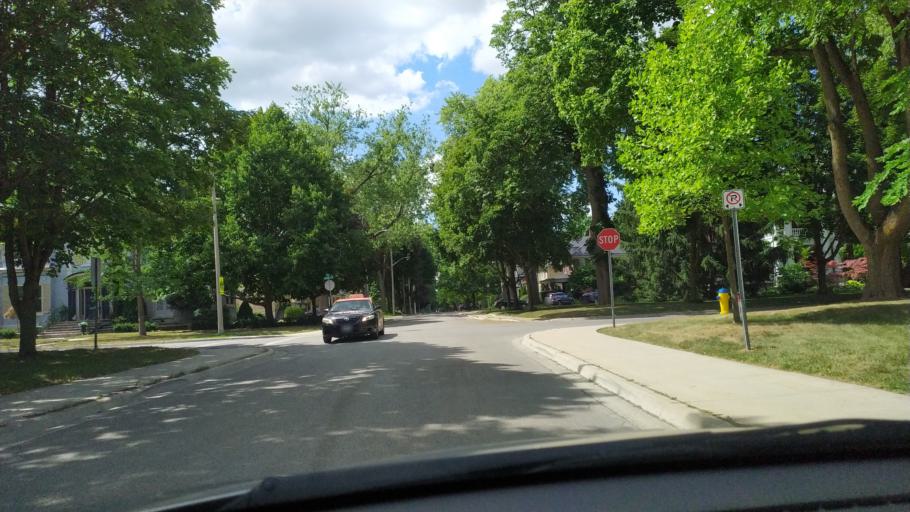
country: CA
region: Ontario
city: Stratford
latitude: 43.3737
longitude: -80.9920
